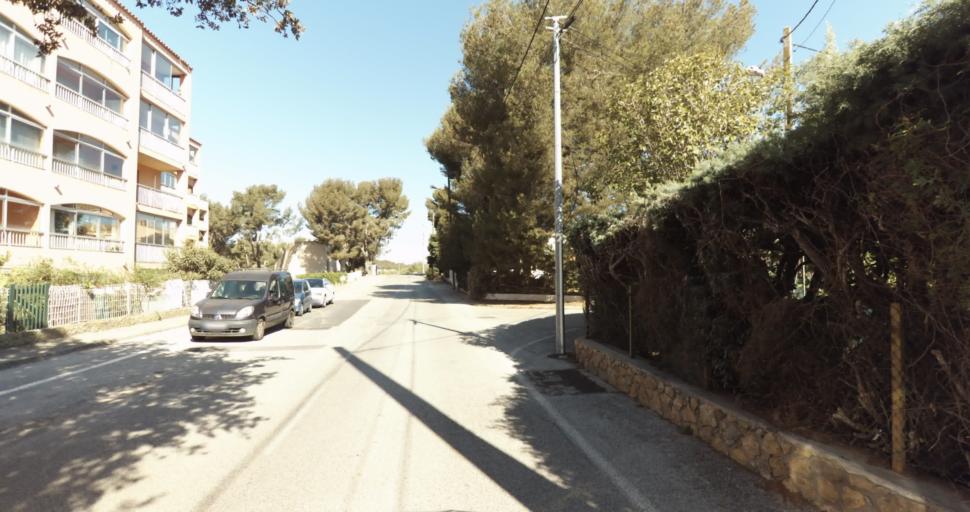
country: FR
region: Provence-Alpes-Cote d'Azur
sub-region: Departement du Var
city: Saint-Mandrier-sur-Mer
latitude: 43.0737
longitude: 5.9118
